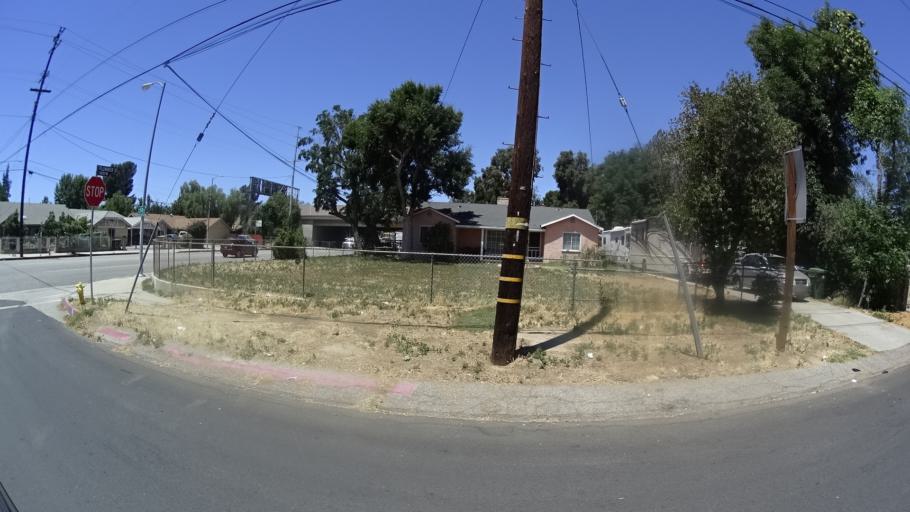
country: US
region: California
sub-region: Los Angeles County
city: San Fernando
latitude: 34.2430
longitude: -118.4719
